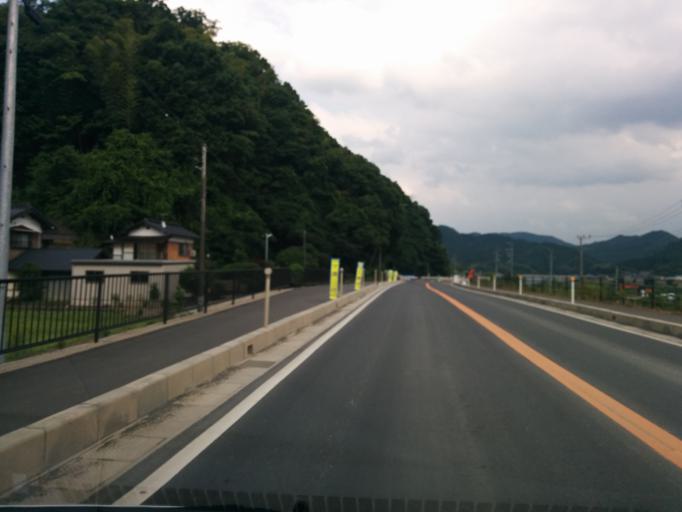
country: JP
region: Kyoto
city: Fukuchiyama
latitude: 35.3949
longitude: 135.1730
